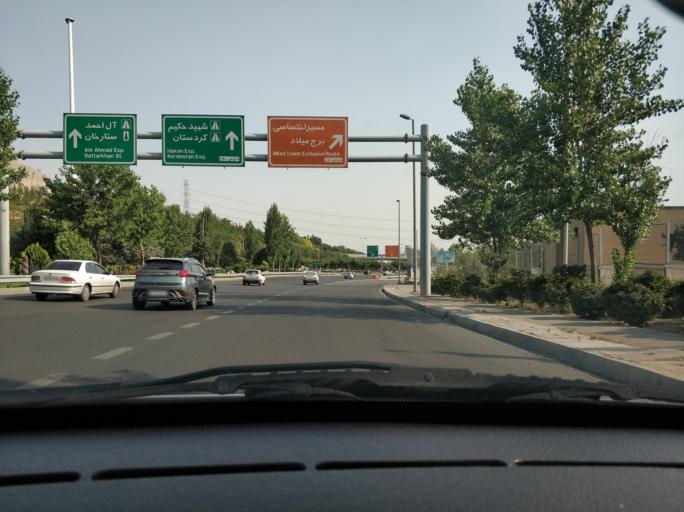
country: IR
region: Tehran
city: Tehran
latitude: 35.7473
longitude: 51.3701
